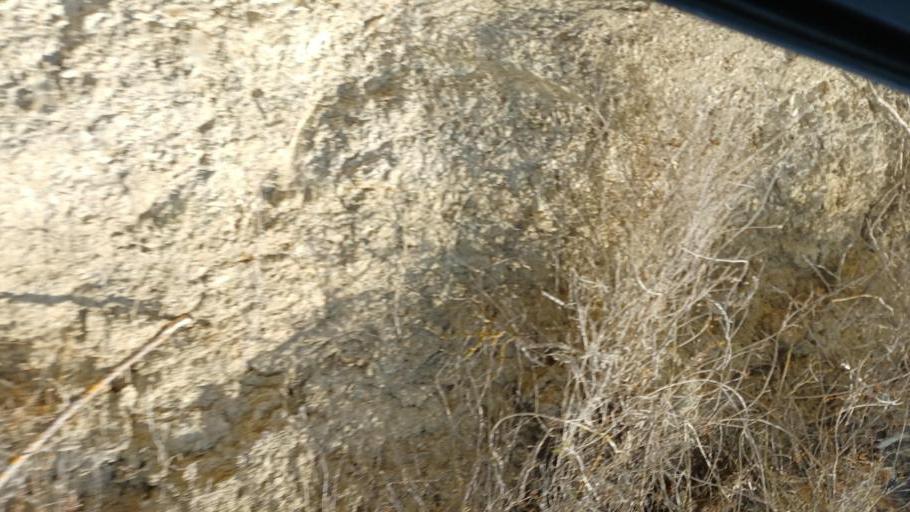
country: CY
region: Pafos
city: Tala
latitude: 34.9373
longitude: 32.4773
